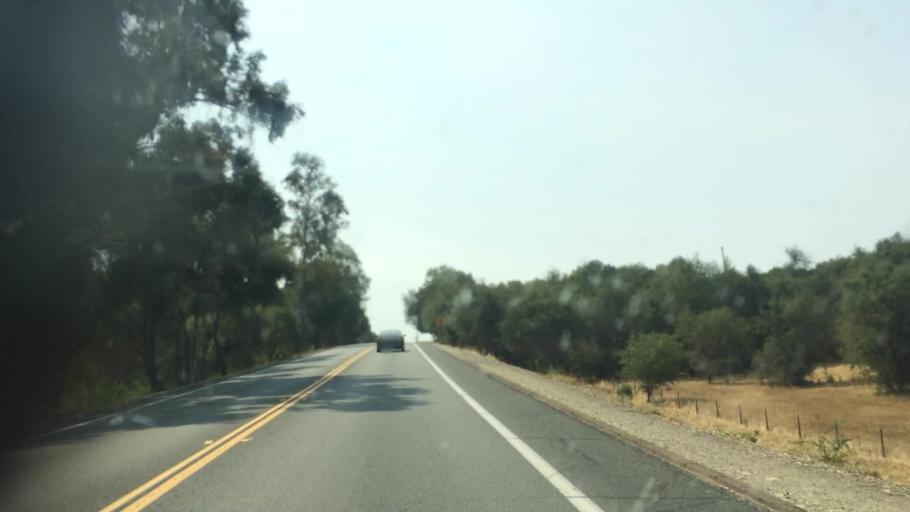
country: US
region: California
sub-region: Amador County
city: Ione
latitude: 38.3612
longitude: -120.9413
